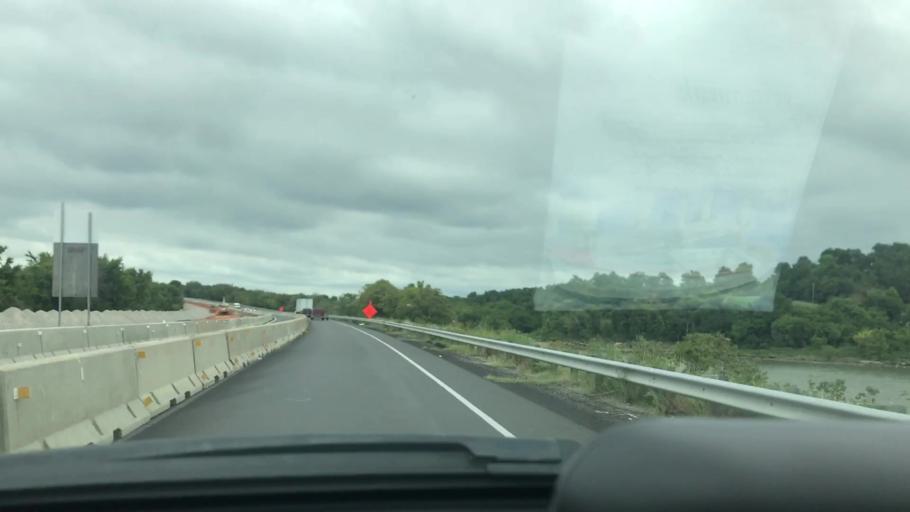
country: US
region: Oklahoma
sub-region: McIntosh County
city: Eufaula
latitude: 35.2466
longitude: -95.5851
